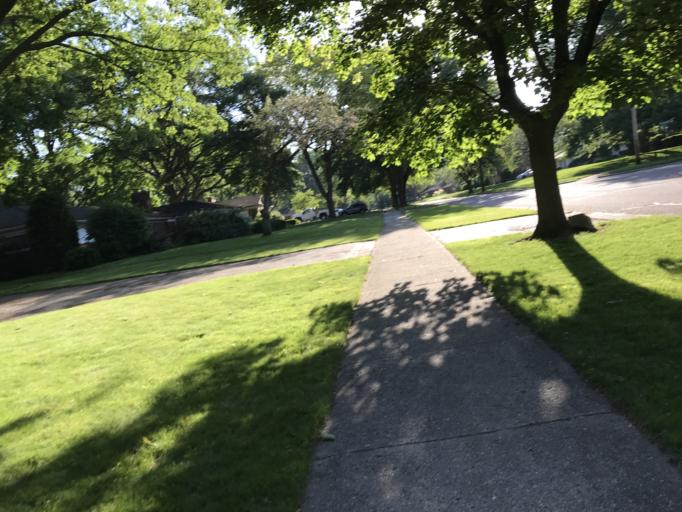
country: US
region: Michigan
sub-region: Oakland County
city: Farmington
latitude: 42.4617
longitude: -83.3822
